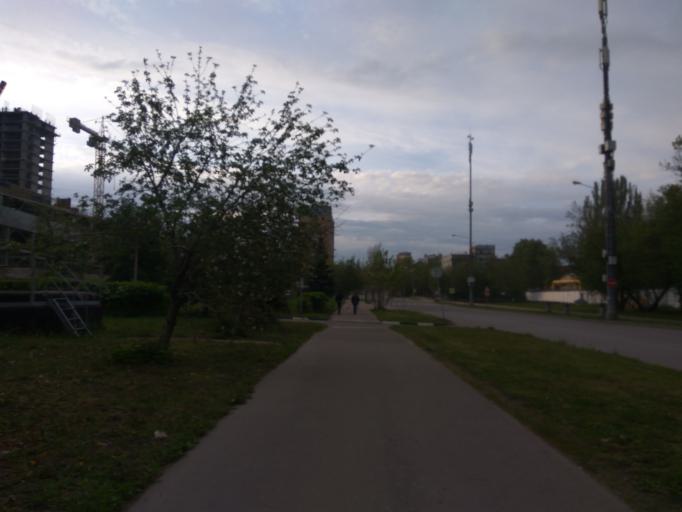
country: RU
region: Moscow
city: Sokol
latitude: 55.7848
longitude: 37.5002
